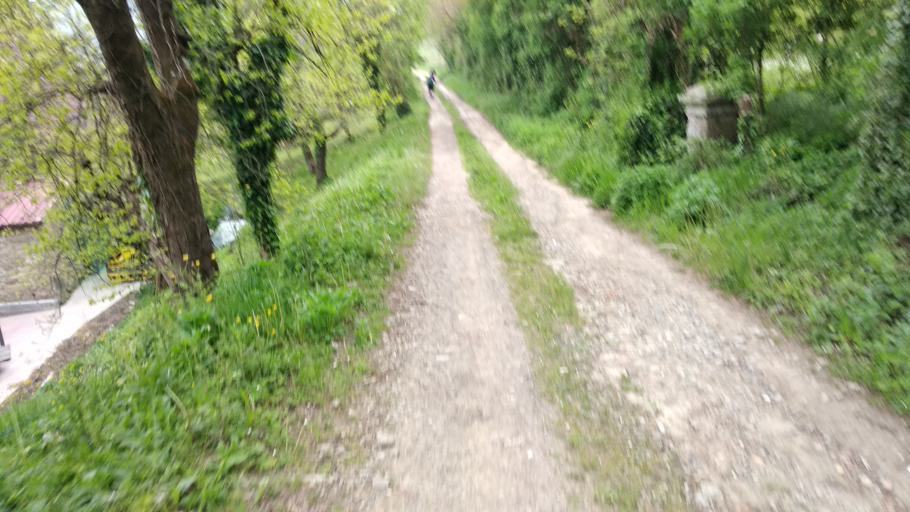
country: IT
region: Emilia-Romagna
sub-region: Forli-Cesena
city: Modigliana
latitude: 44.1478
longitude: 11.7979
